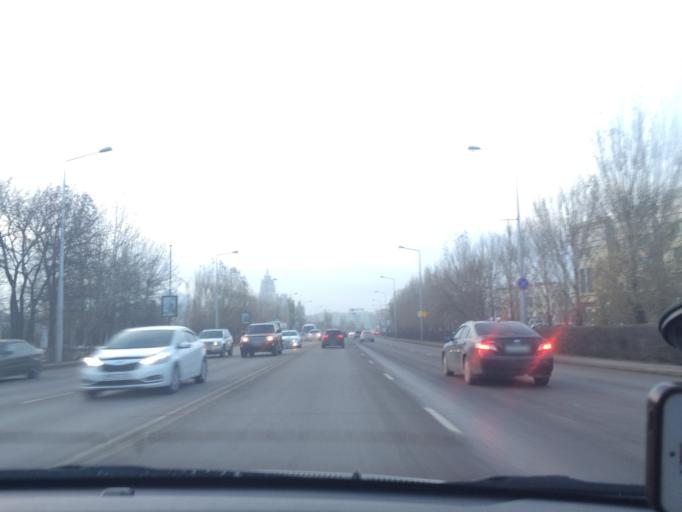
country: KZ
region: Astana Qalasy
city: Astana
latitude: 51.1516
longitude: 71.4126
